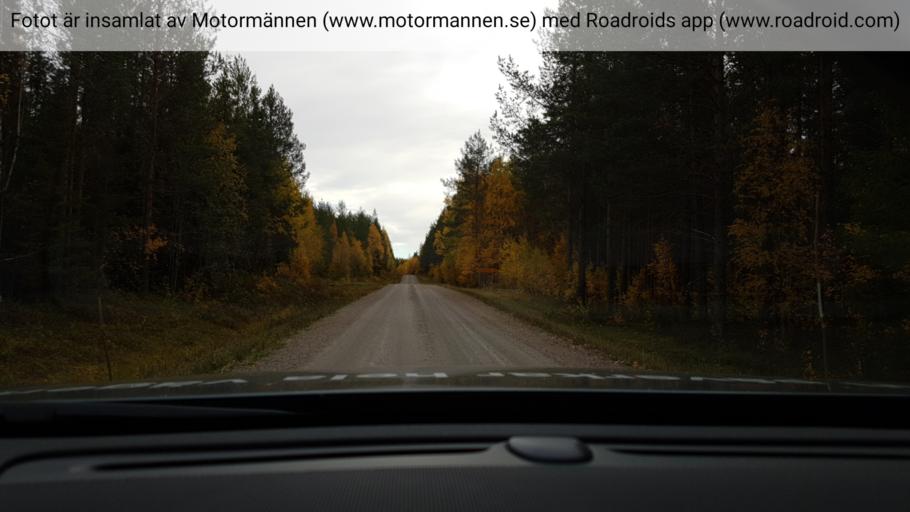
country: SE
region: Norrbotten
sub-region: Overkalix Kommun
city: OEverkalix
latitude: 66.2777
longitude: 22.9827
